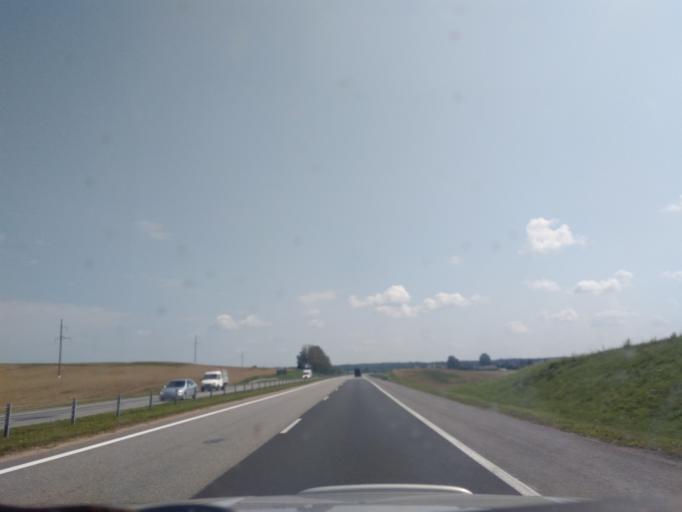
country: BY
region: Minsk
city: Novosel'ye
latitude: 53.9154
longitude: 27.2288
